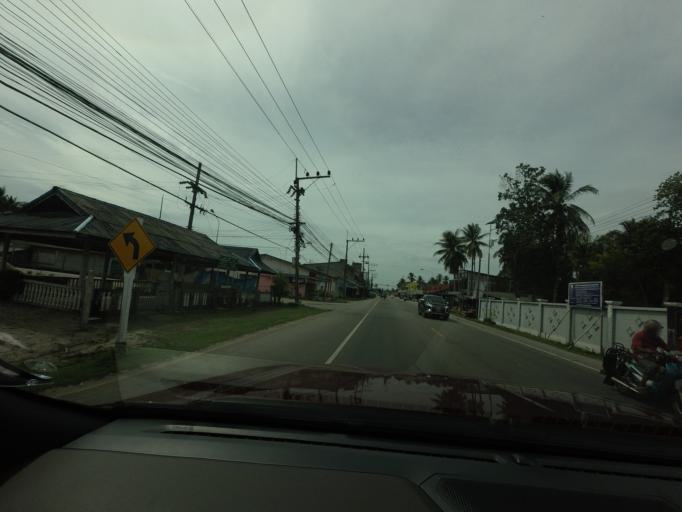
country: TH
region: Narathiwat
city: Tak Bai
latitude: 6.2391
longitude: 102.0821
